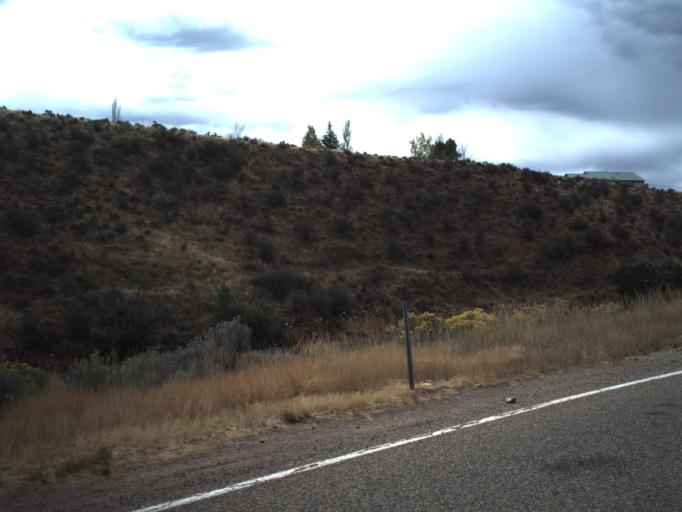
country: US
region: Utah
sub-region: Morgan County
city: Morgan
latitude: 40.9257
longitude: -111.5937
